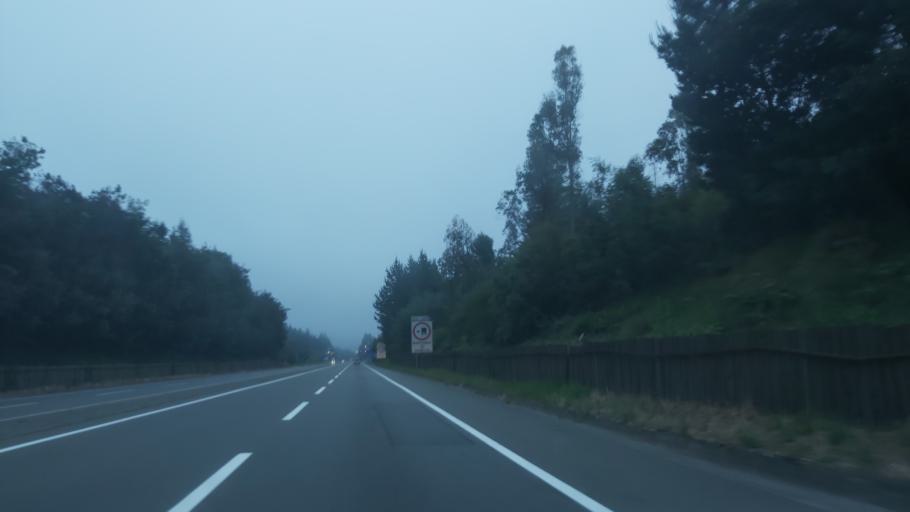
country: CL
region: Biobio
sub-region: Provincia de Concepcion
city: Penco
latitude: -36.7324
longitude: -72.8821
